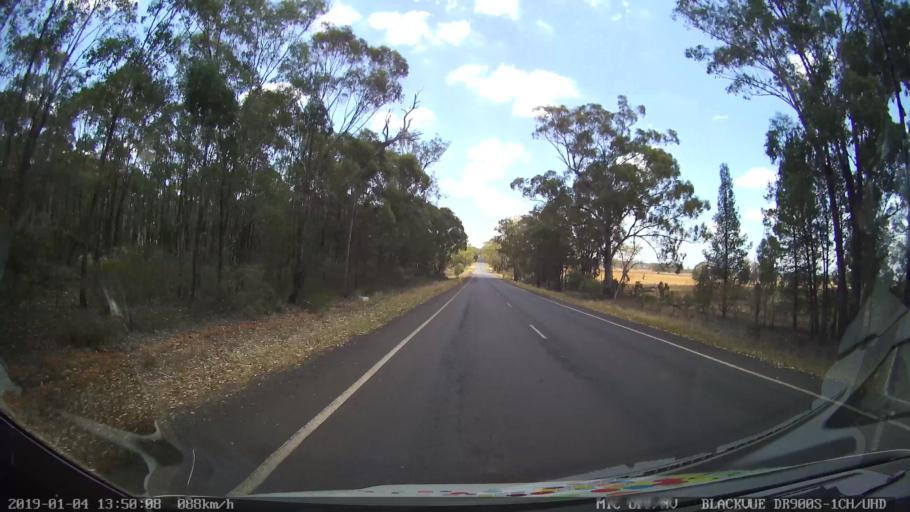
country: AU
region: New South Wales
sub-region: Dubbo Municipality
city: Dubbo
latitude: -32.4236
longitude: 148.5748
